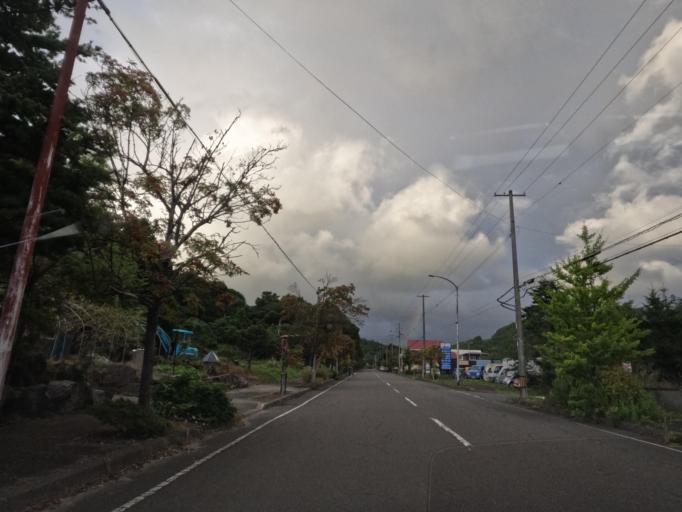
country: JP
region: Hokkaido
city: Muroran
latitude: 42.3712
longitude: 140.9550
